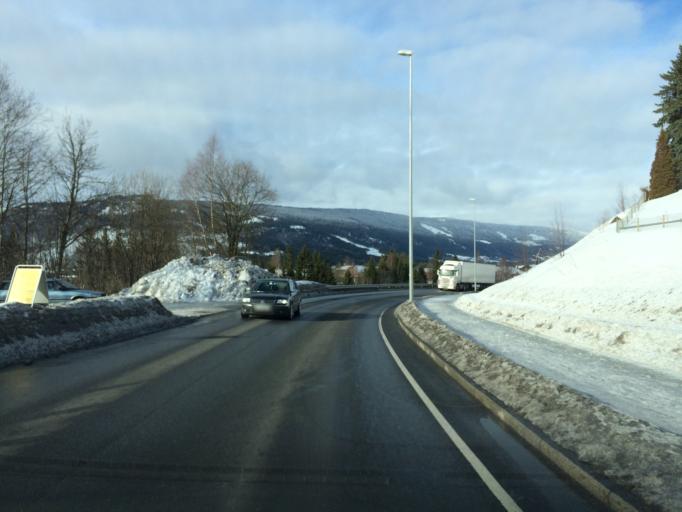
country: NO
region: Oppland
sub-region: Gausdal
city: Segalstad bru
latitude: 61.2253
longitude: 10.2296
